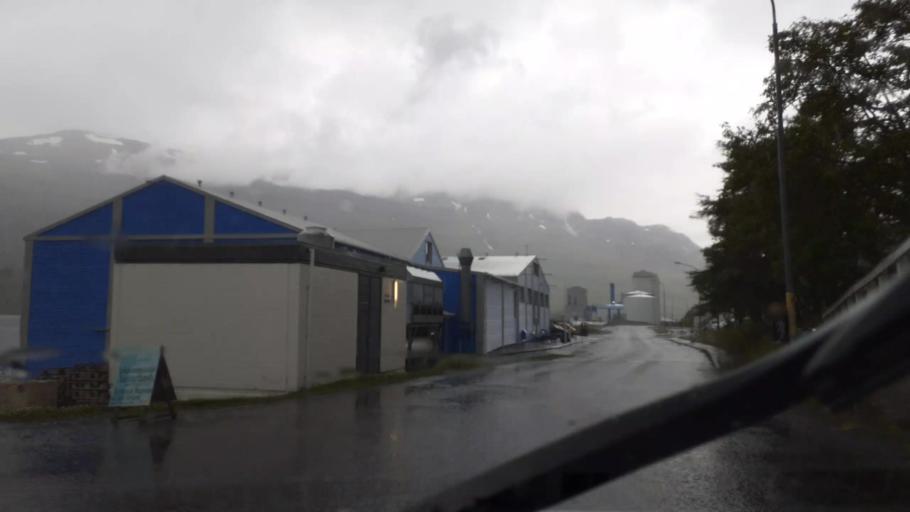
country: IS
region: East
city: Eskifjoerdur
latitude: 65.2662
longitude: -13.9914
